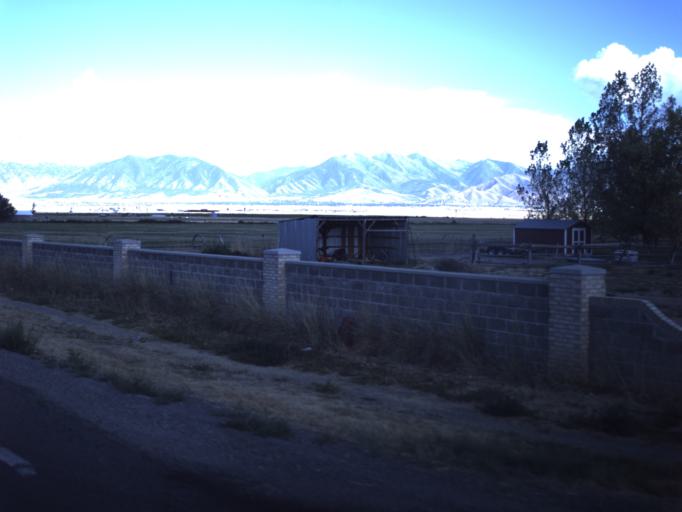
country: US
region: Utah
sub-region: Tooele County
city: Grantsville
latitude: 40.5996
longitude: -112.4213
